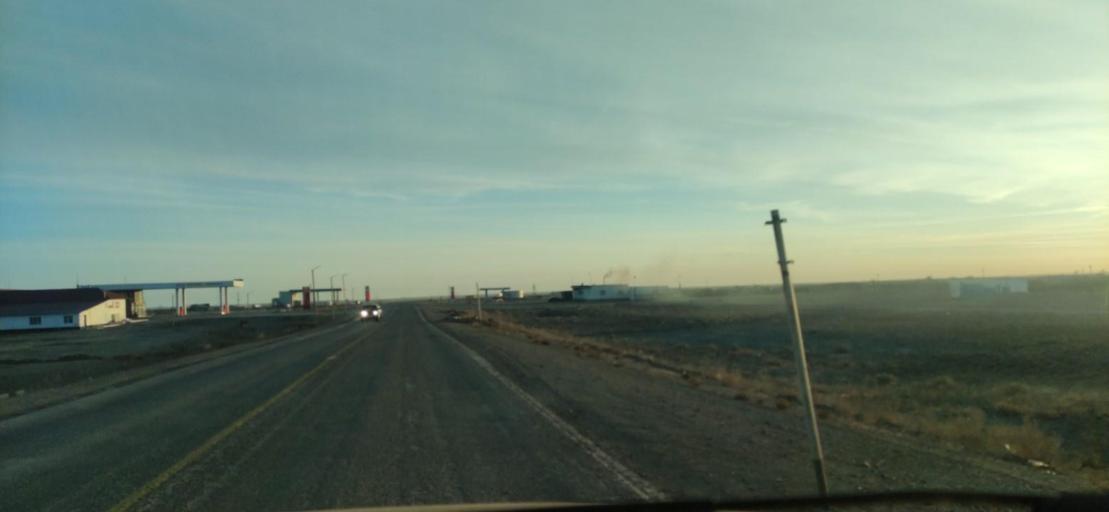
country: KZ
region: Qaraghandy
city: Saryshaghan
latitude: 46.0233
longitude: 73.5913
